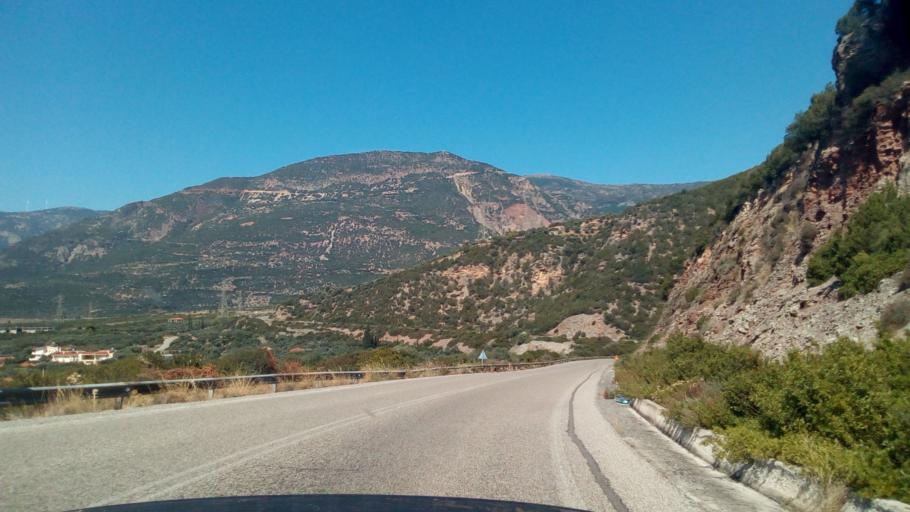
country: GR
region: West Greece
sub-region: Nomos Achaias
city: Selianitika
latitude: 38.3717
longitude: 22.0973
